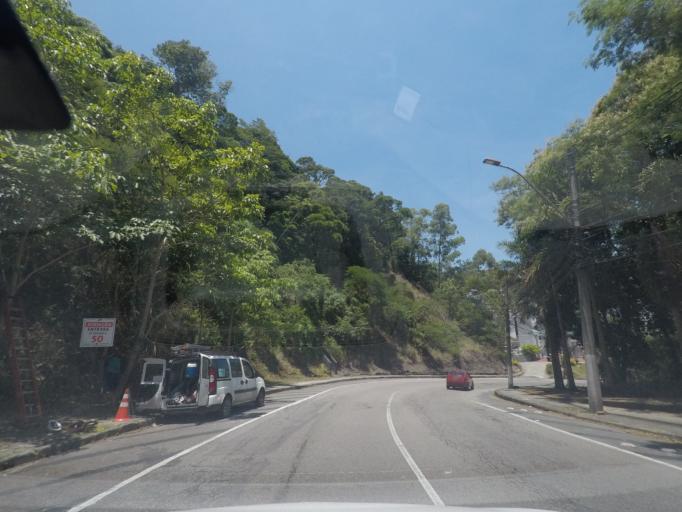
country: BR
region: Rio de Janeiro
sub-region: Niteroi
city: Niteroi
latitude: -22.9194
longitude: -43.0639
